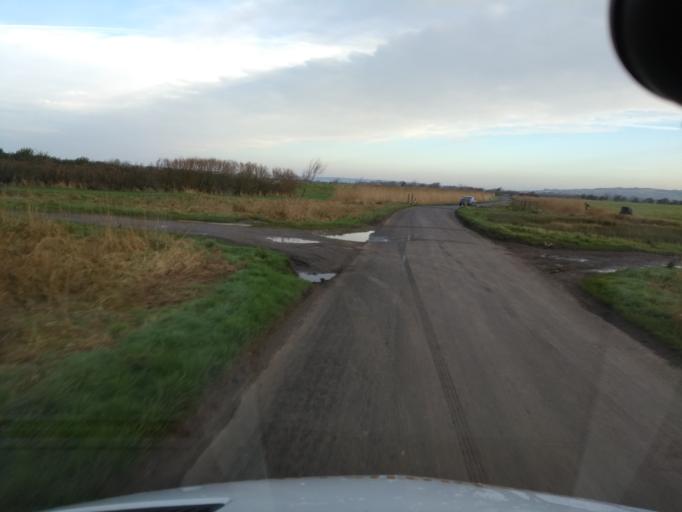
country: GB
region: England
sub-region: Somerset
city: Burnham-on-Sea
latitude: 51.2791
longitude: -3.0013
